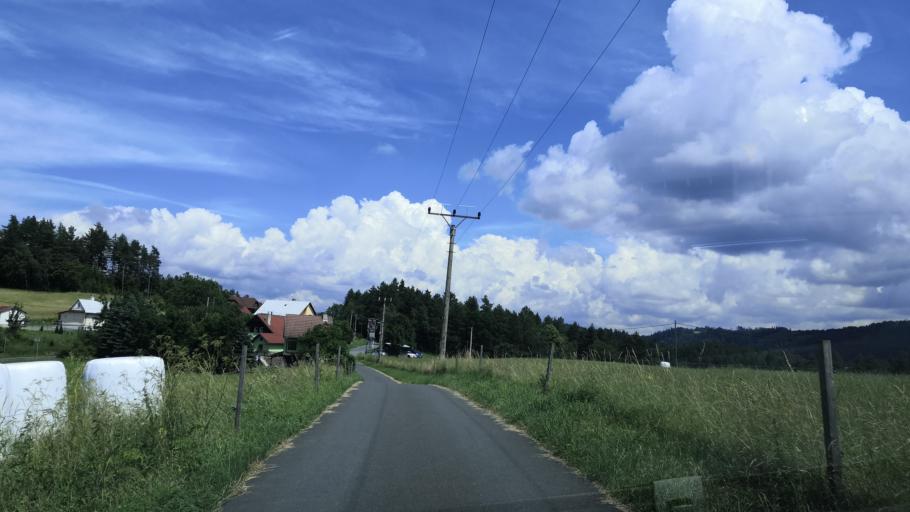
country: CZ
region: Zlin
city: Vidce
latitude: 49.4275
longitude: 18.0990
